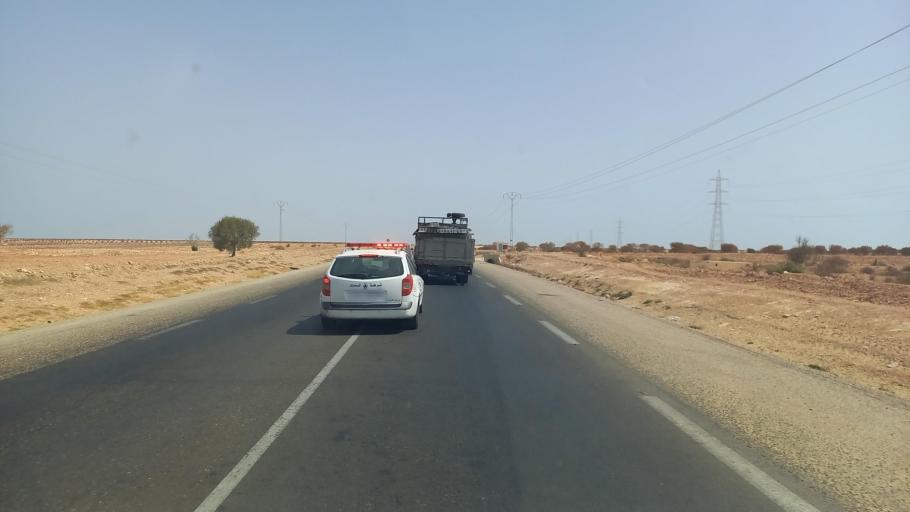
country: TN
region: Madanin
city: Zarzis
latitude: 33.4059
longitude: 10.8587
